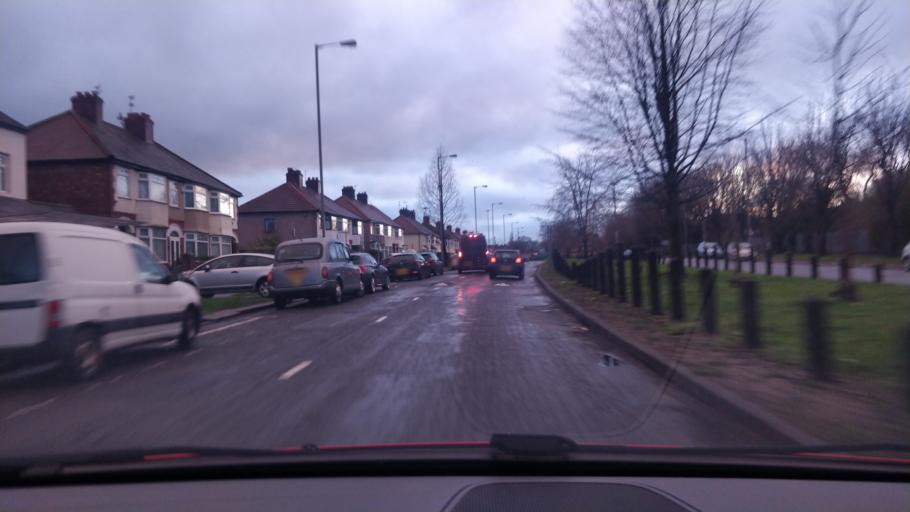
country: GB
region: England
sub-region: Knowsley
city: Huyton
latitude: 53.4097
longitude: -2.8973
